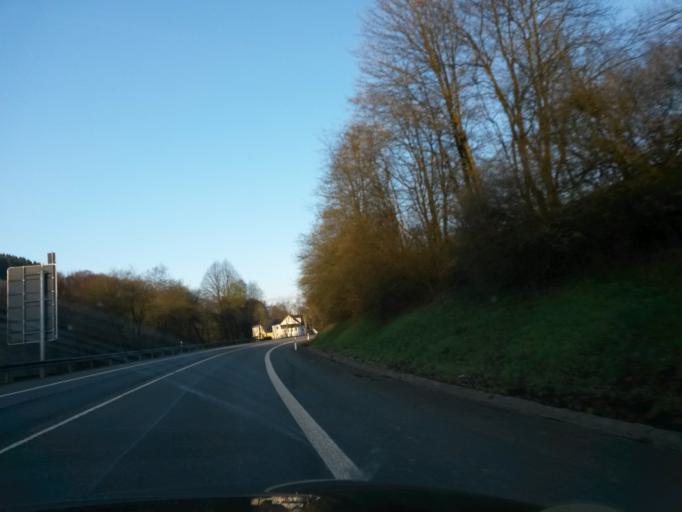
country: DE
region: North Rhine-Westphalia
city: Meinerzhagen
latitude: 51.1058
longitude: 7.7081
